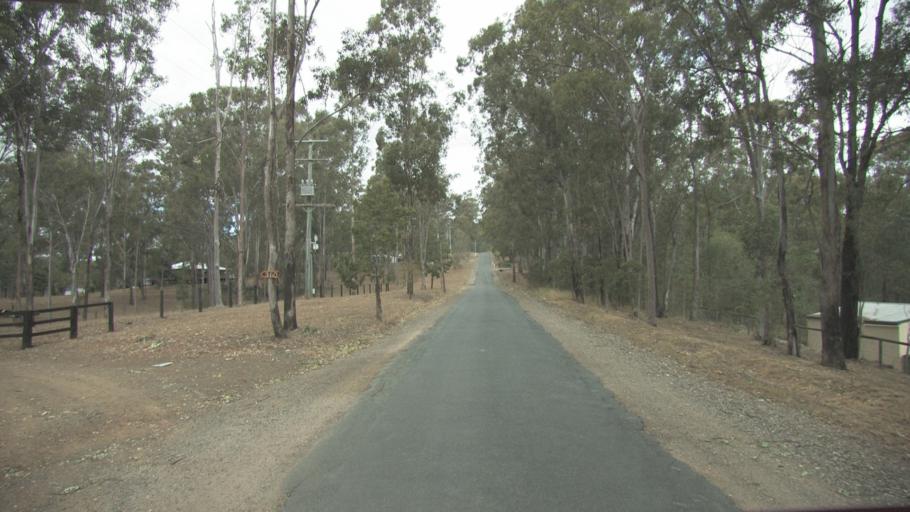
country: AU
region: Queensland
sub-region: Logan
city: Cedar Vale
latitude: -27.8909
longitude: 153.0313
